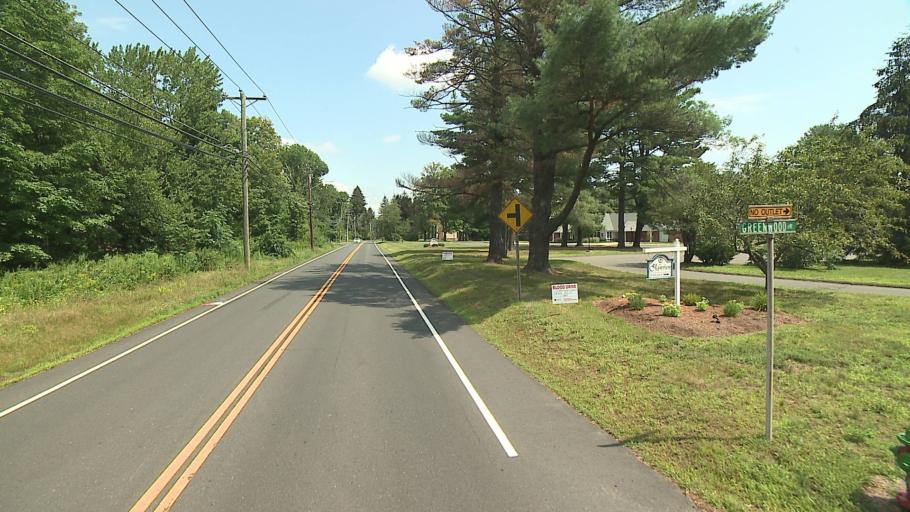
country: US
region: Connecticut
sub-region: Hartford County
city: Collinsville
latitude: 41.7986
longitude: -72.8901
